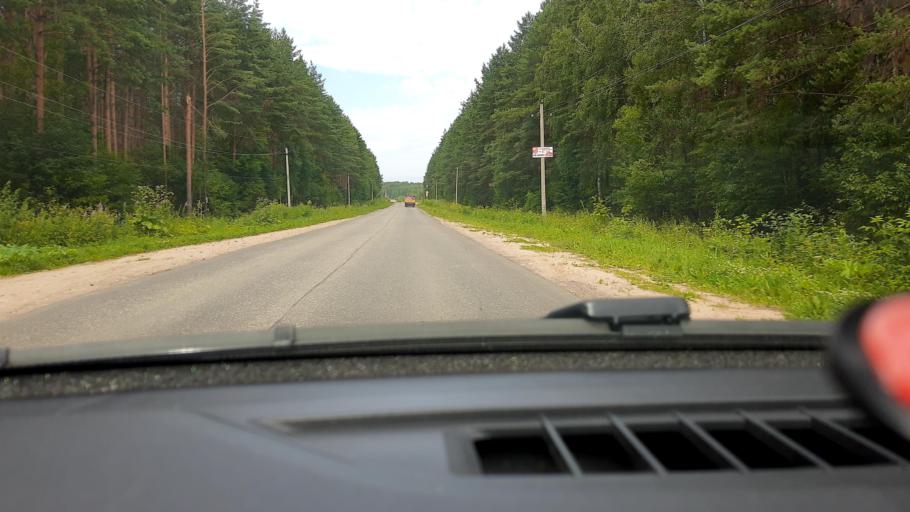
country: RU
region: Nizjnij Novgorod
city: Bogorodsk
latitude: 56.1313
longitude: 43.5932
